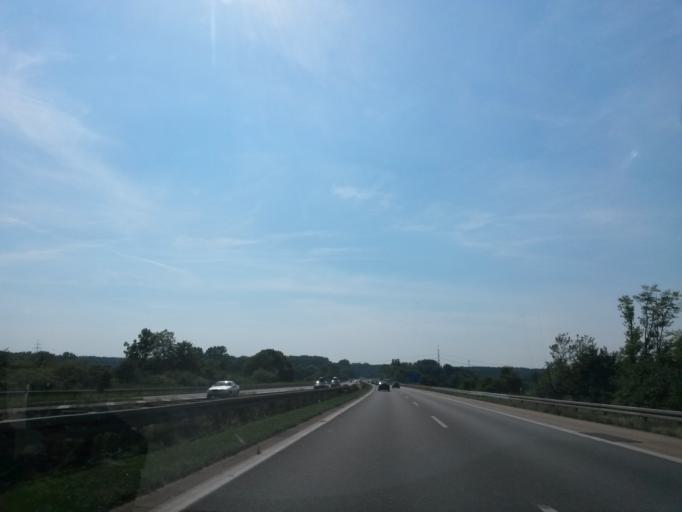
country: DE
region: Bavaria
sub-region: Regierungsbezirk Unterfranken
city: Wiesentheid
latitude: 49.7751
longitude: 10.3412
